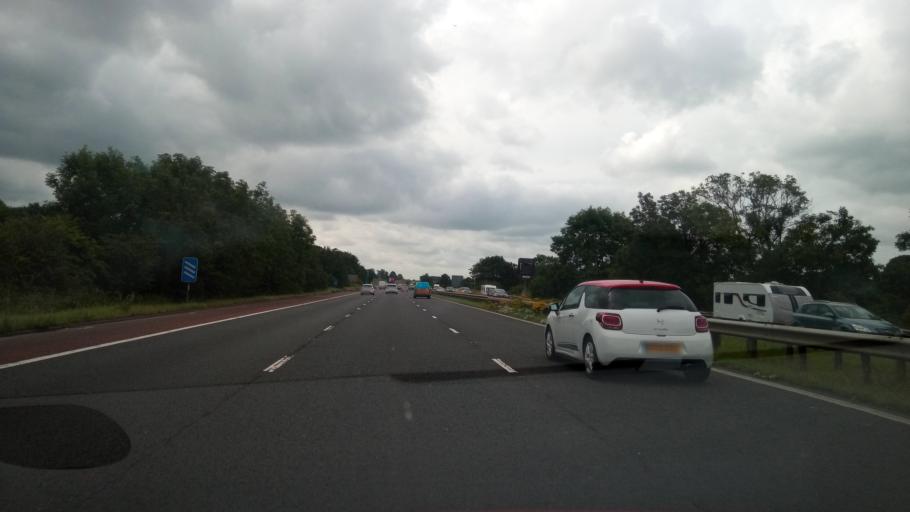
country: GB
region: England
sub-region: Lancashire
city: Galgate
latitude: 53.9920
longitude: -2.7809
